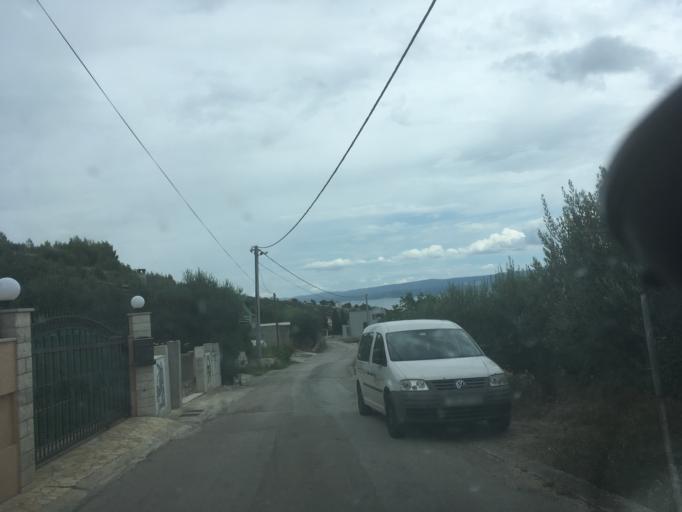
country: HR
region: Splitsko-Dalmatinska
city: Jesenice
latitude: 43.4566
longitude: 16.6212
